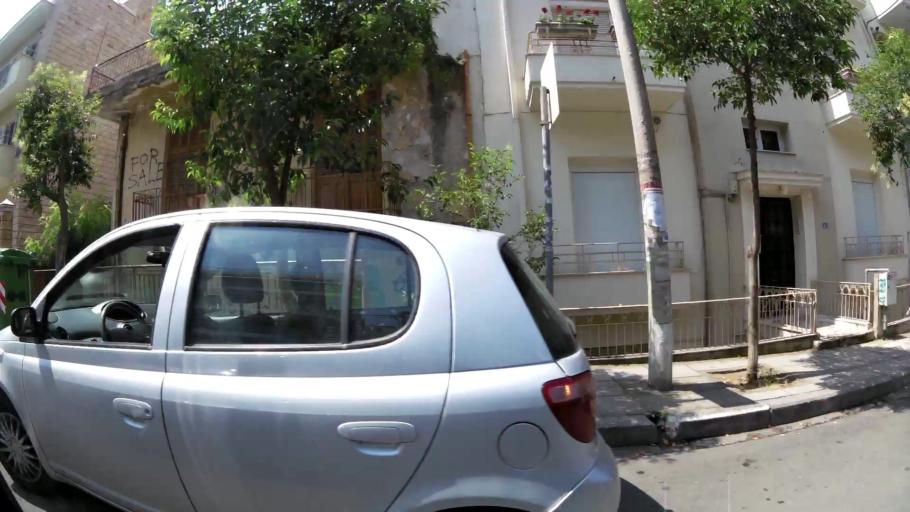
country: GR
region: Central Macedonia
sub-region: Nomos Thessalonikis
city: Agios Pavlos
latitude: 40.6327
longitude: 22.9628
